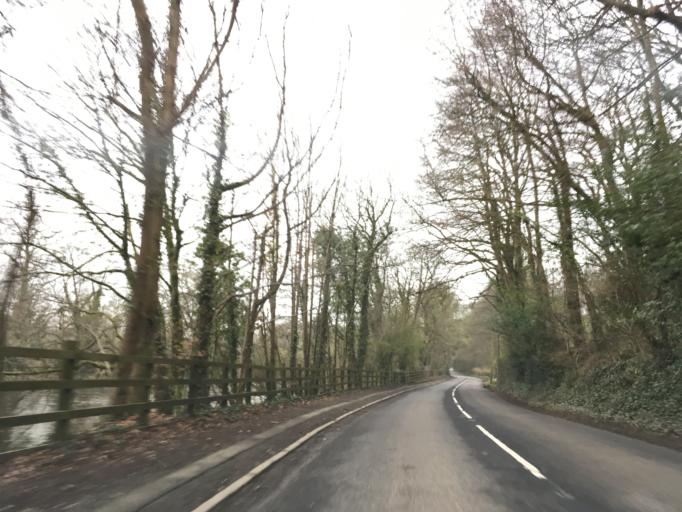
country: GB
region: Wales
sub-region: Monmouthshire
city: Usk
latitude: 51.7117
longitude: -2.9094
